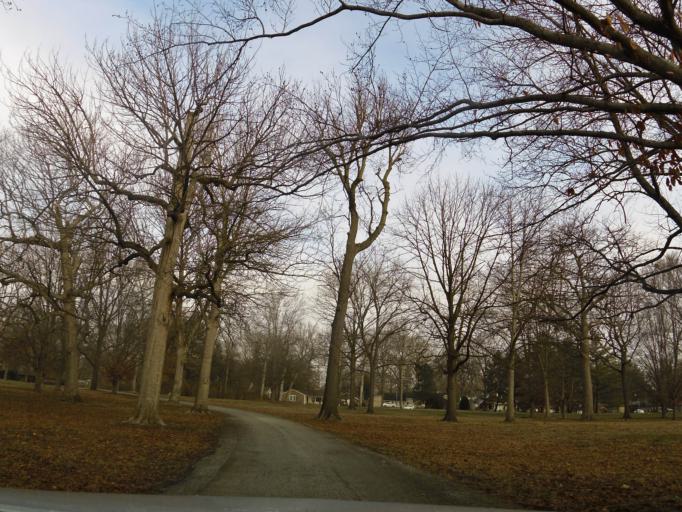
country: US
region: Indiana
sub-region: Bartholomew County
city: Columbus
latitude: 39.2294
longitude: -85.9136
